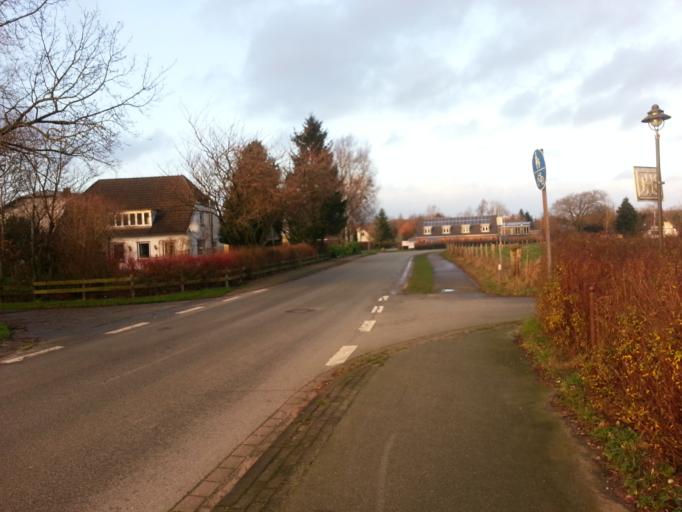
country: DE
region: Schleswig-Holstein
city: Maasbull
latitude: 54.7756
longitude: 9.5243
